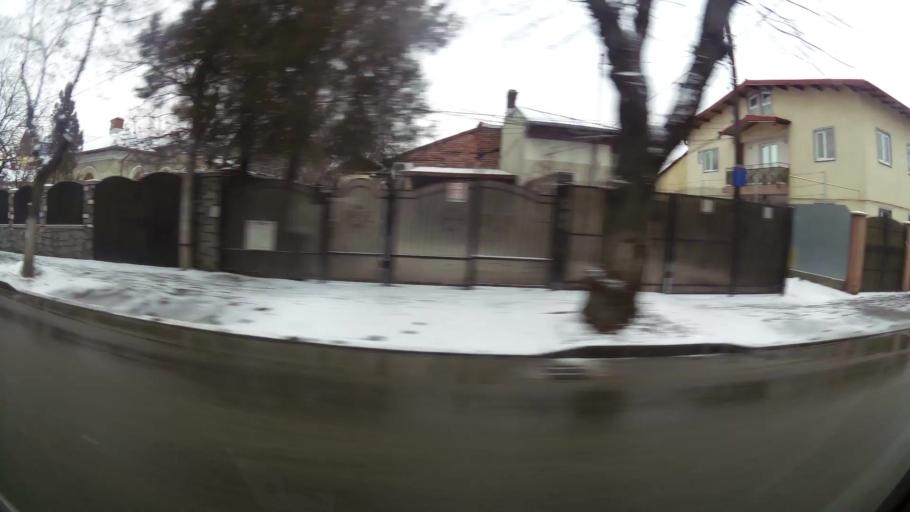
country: RO
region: Prahova
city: Ploiesti
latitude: 44.9349
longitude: 26.0459
